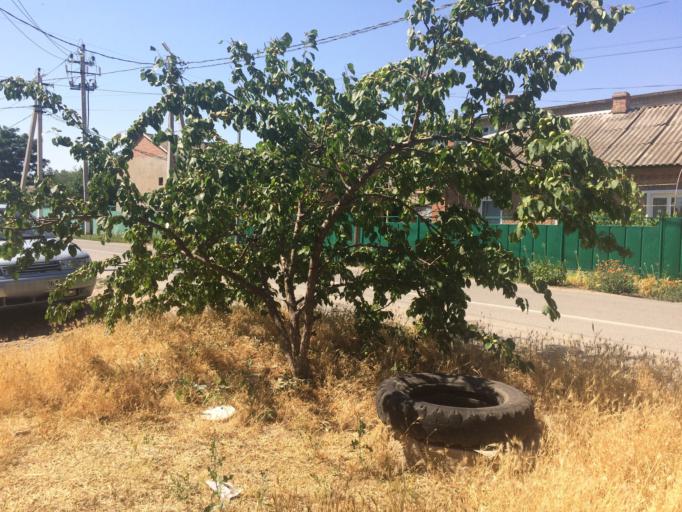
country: RU
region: Rostov
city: Sal'sk
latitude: 46.4763
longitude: 41.5464
